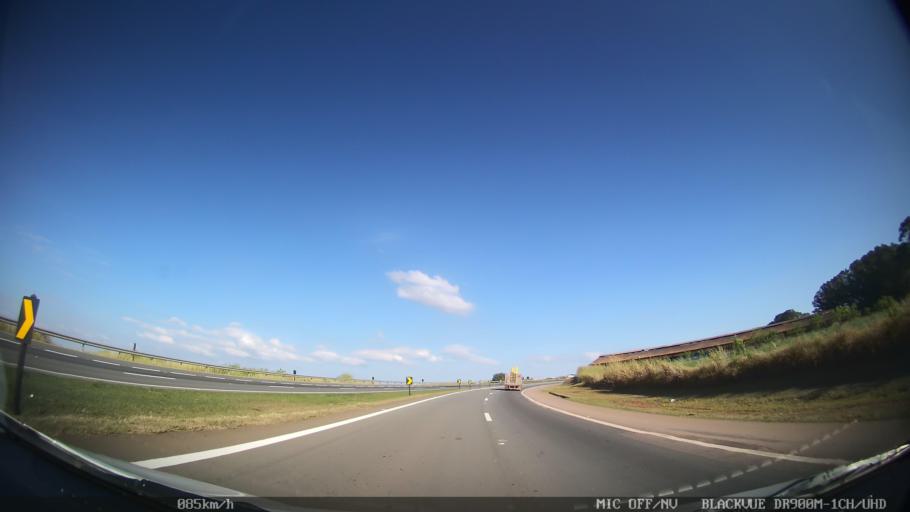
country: BR
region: Sao Paulo
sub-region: Piracicaba
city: Piracicaba
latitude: -22.7167
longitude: -47.6063
